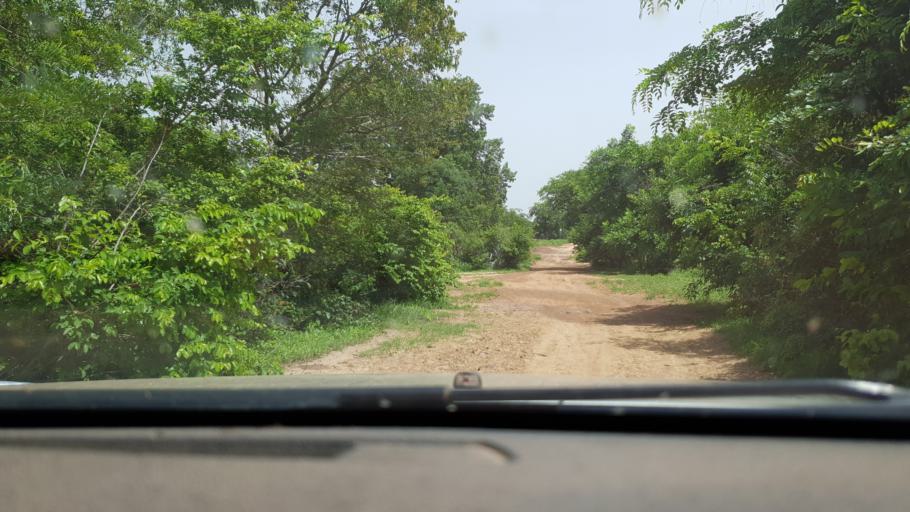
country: ML
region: Koulikoro
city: Koulikoro
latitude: 12.6689
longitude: -7.2448
